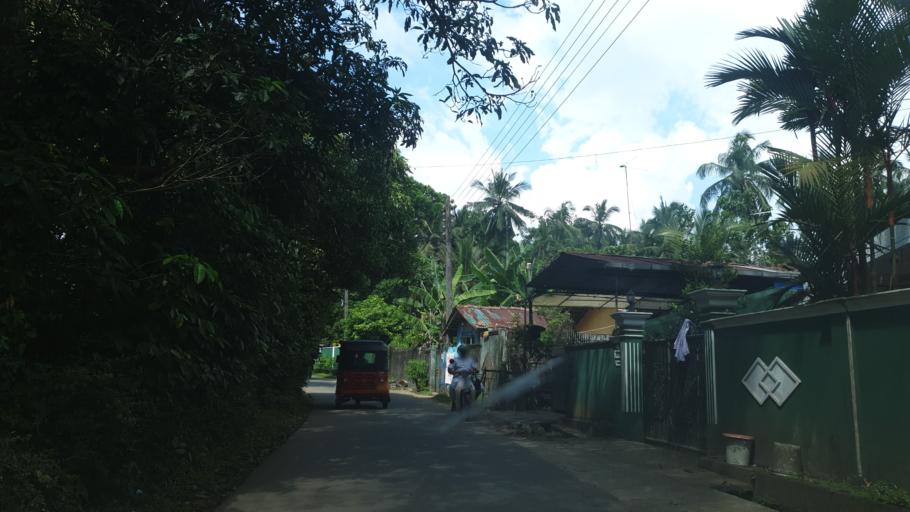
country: LK
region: Western
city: Horana South
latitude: 6.7042
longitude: 79.9852
